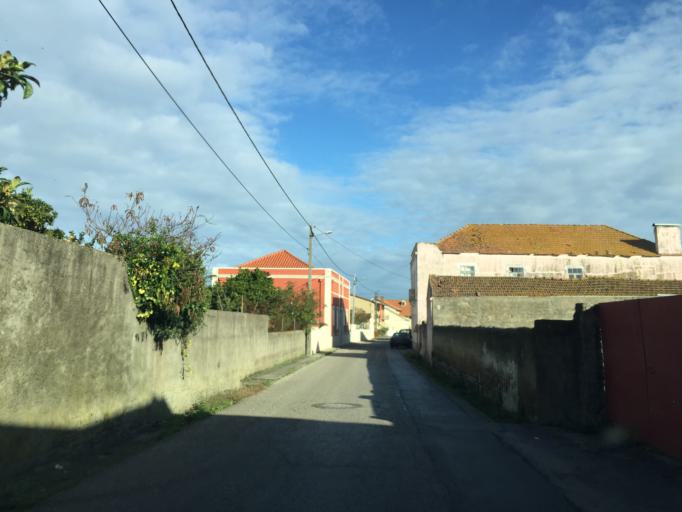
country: PT
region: Coimbra
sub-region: Figueira da Foz
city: Lavos
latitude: 40.0682
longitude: -8.8202
